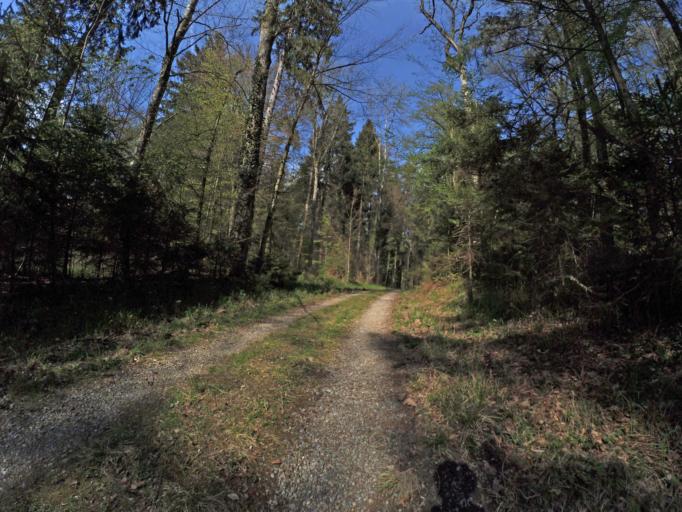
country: CH
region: Thurgau
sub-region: Frauenfeld District
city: Diessenhofen
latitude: 47.6499
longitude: 8.7478
